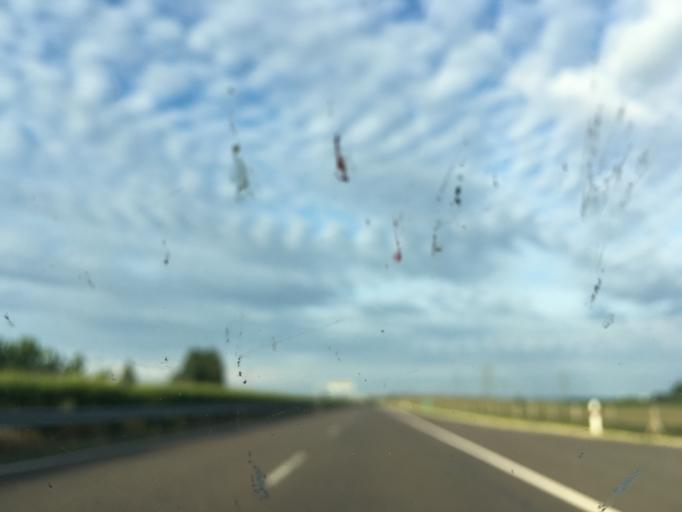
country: HU
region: Hajdu-Bihar
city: Debrecen
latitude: 47.5632
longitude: 21.5578
